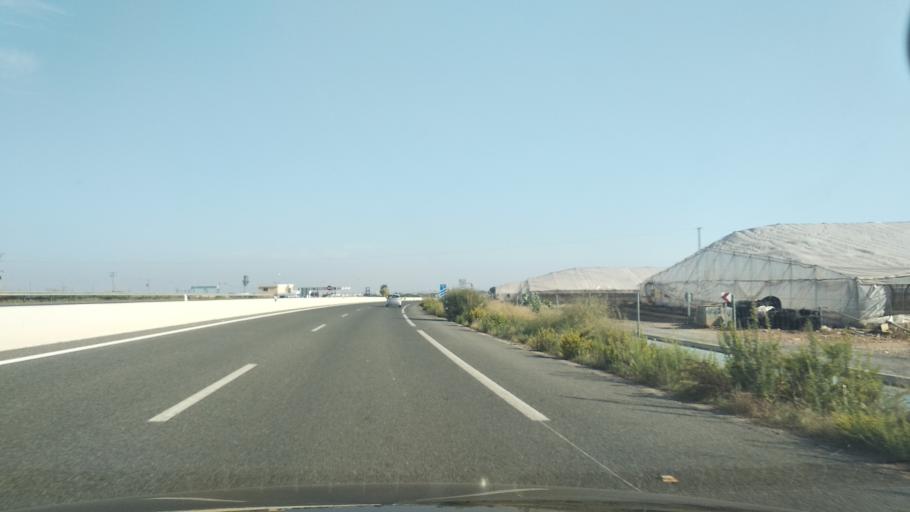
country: ES
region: Murcia
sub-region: Murcia
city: San Javier
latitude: 37.8543
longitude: -0.8829
